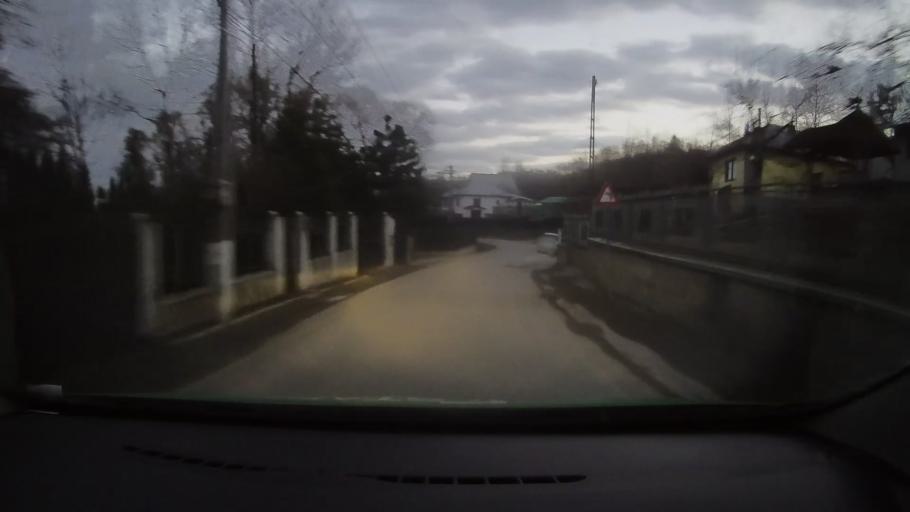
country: RO
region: Prahova
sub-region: Comuna Provita de Sus
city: Provita de Sus
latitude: 45.1391
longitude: 25.6309
